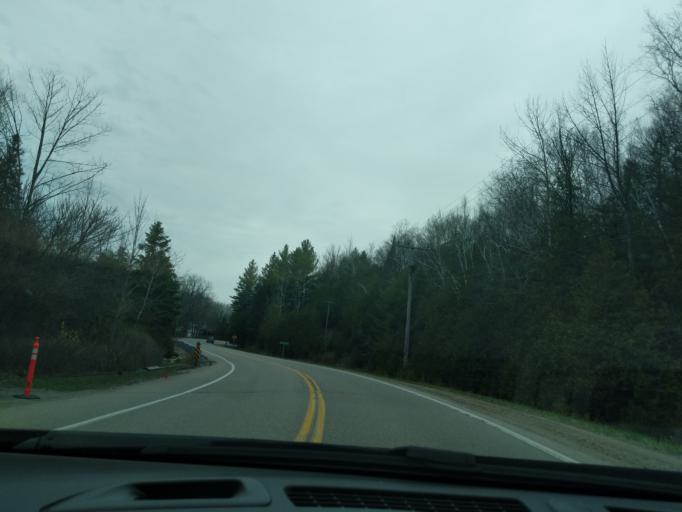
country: CA
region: Ontario
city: Orangeville
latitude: 44.0002
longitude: -80.0007
